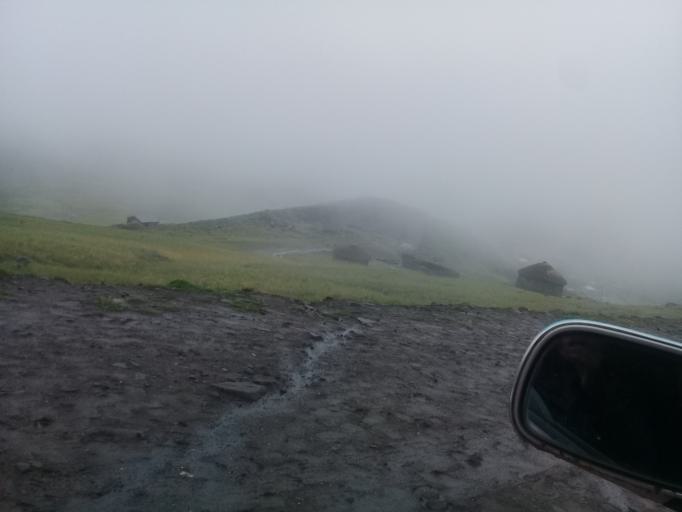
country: LS
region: Mokhotlong
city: Mokhotlong
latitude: -29.3772
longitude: 28.9860
